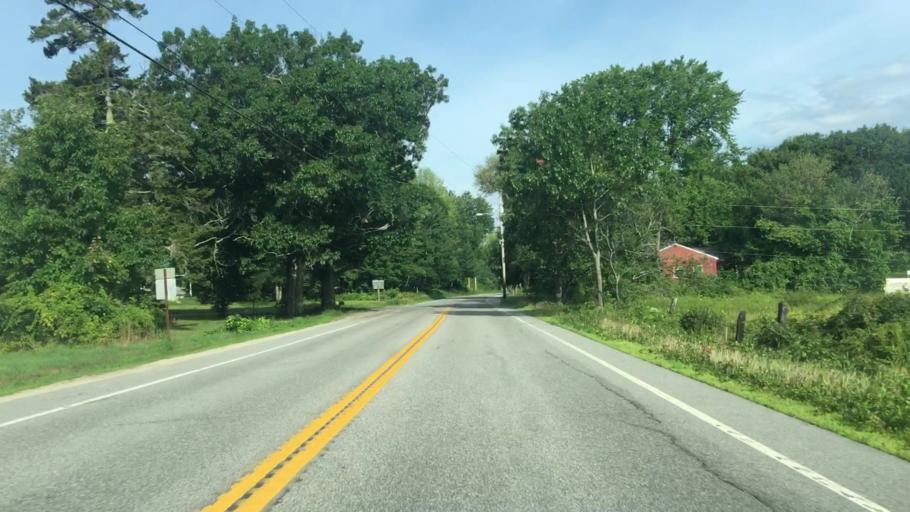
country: US
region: Maine
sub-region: York County
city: Cornish
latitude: 43.7809
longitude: -70.7539
